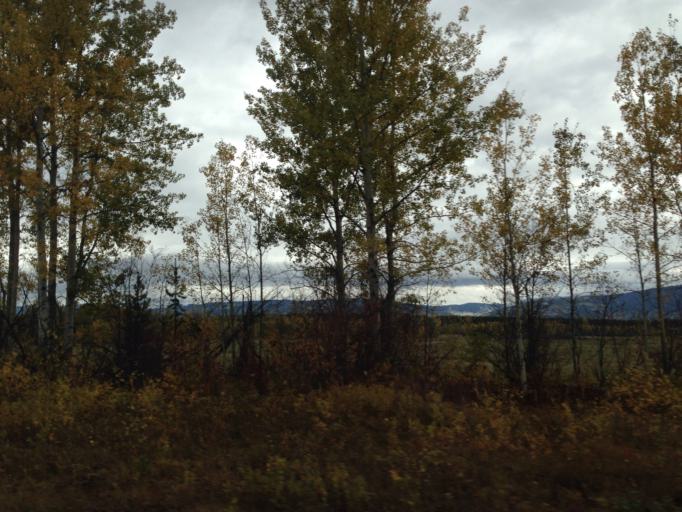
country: CA
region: British Columbia
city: Smithers
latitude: 54.8760
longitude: -127.2558
